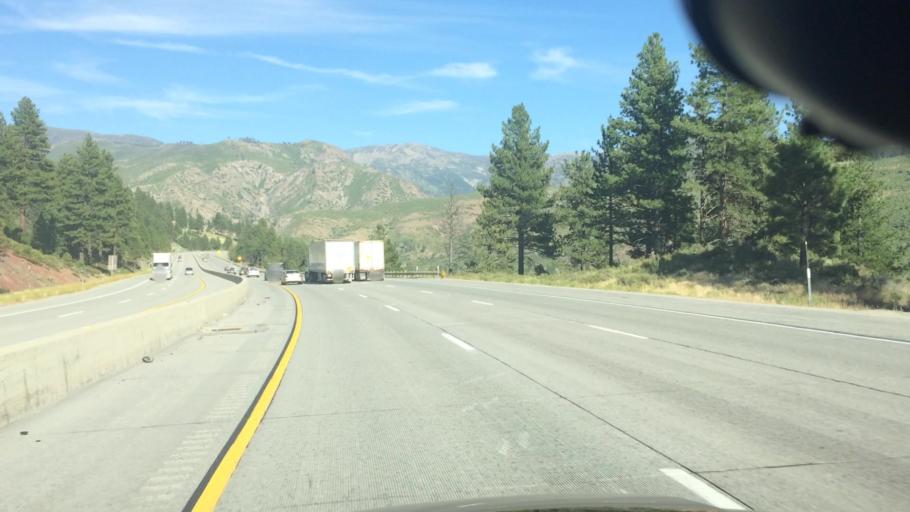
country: US
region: California
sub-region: Nevada County
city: Truckee
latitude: 39.3732
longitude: -120.0630
